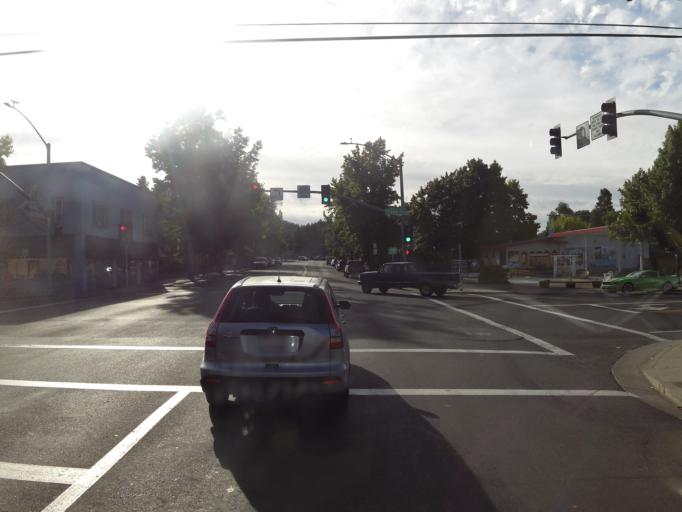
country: US
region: California
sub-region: Siskiyou County
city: Mount Shasta
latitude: 41.3134
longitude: -122.3125
